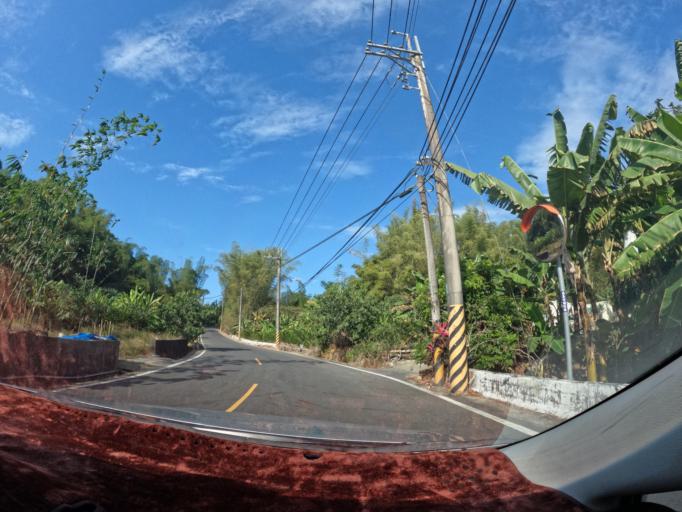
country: TW
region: Taiwan
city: Yujing
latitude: 23.0204
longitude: 120.3976
